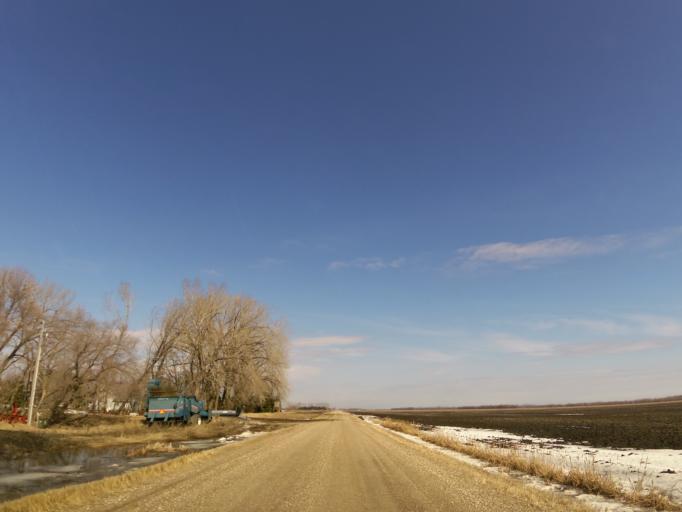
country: US
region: North Dakota
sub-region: Walsh County
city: Grafton
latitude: 48.4063
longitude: -97.1685
